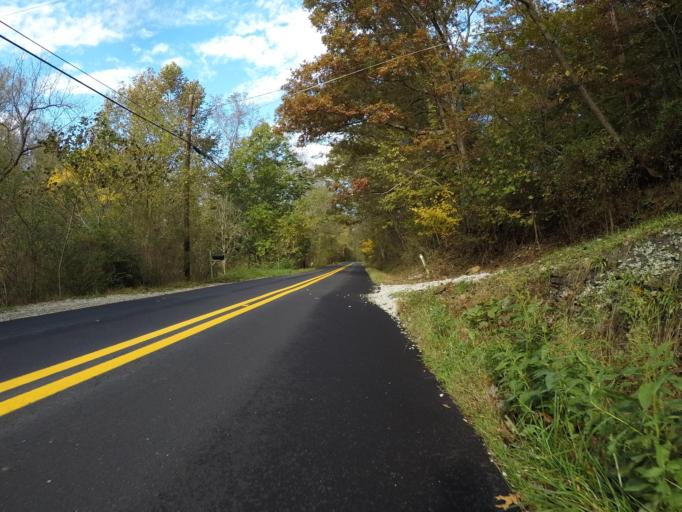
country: US
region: West Virginia
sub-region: Wayne County
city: Lavalette
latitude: 38.3670
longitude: -82.4307
